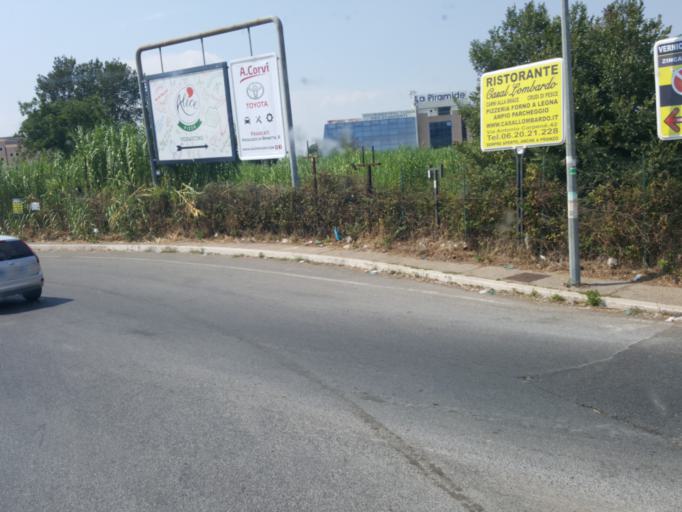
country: IT
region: Latium
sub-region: Citta metropolitana di Roma Capitale
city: Frascati
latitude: 41.8368
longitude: 12.6590
